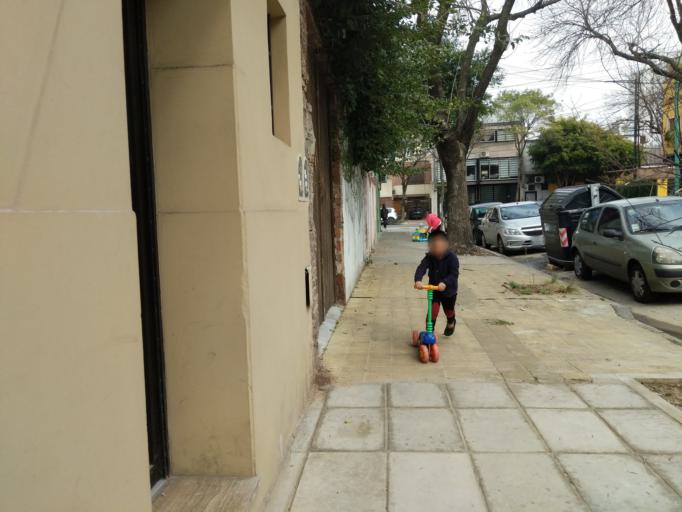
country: AR
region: Buenos Aires F.D.
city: Colegiales
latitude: -34.5866
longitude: -58.4447
